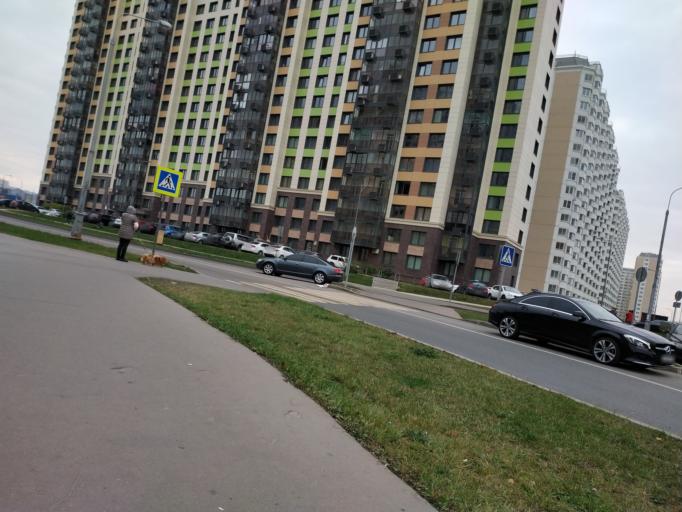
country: RU
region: Moscow
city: Novo-Peredelkino
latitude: 55.6355
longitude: 37.3319
